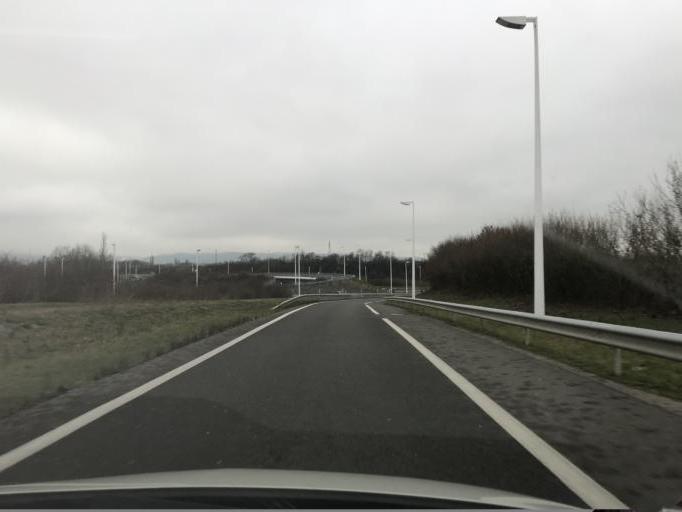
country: FR
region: Rhone-Alpes
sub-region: Departement de la Haute-Savoie
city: Neydens
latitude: 46.1347
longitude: 6.0986
